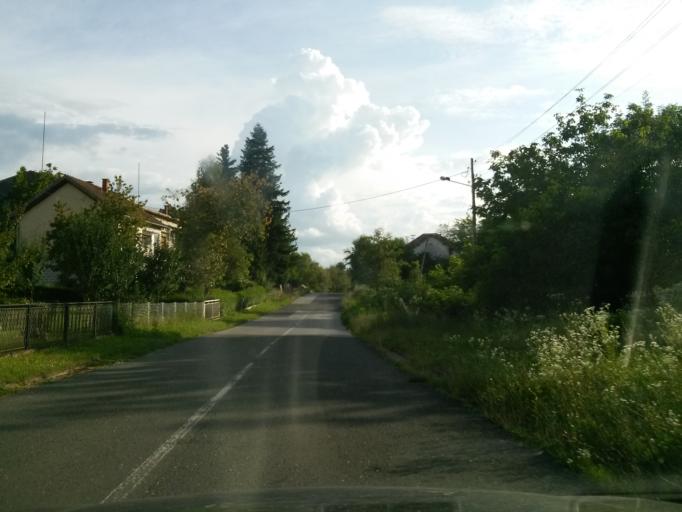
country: HR
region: Sisacko-Moslavacka
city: Gvozd
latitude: 45.4021
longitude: 15.9293
